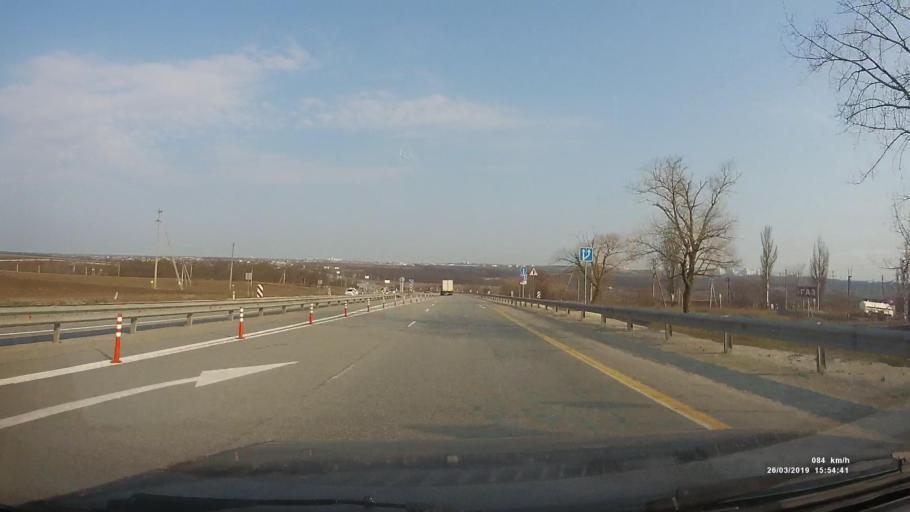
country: RU
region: Rostov
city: Kalinin
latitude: 47.2680
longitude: 39.5620
